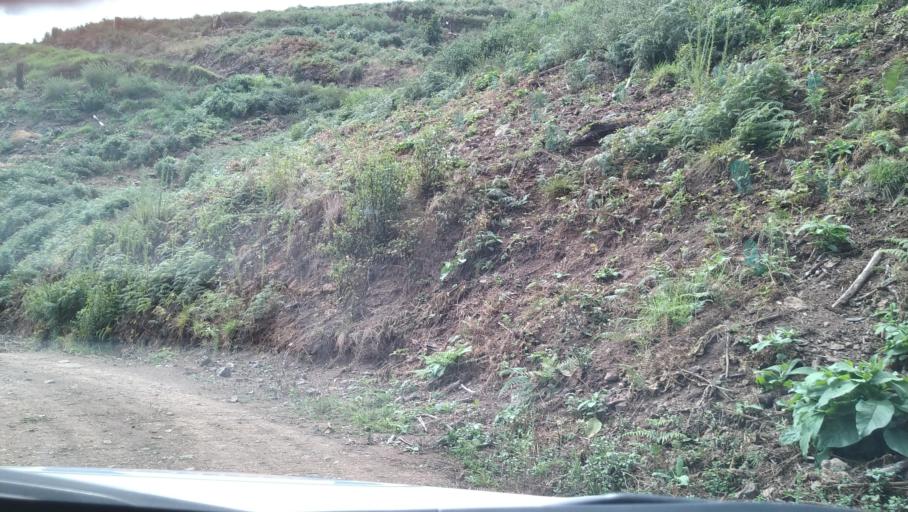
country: PT
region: Madeira
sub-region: Funchal
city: Nossa Senhora do Monte
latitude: 32.6811
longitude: -16.9269
